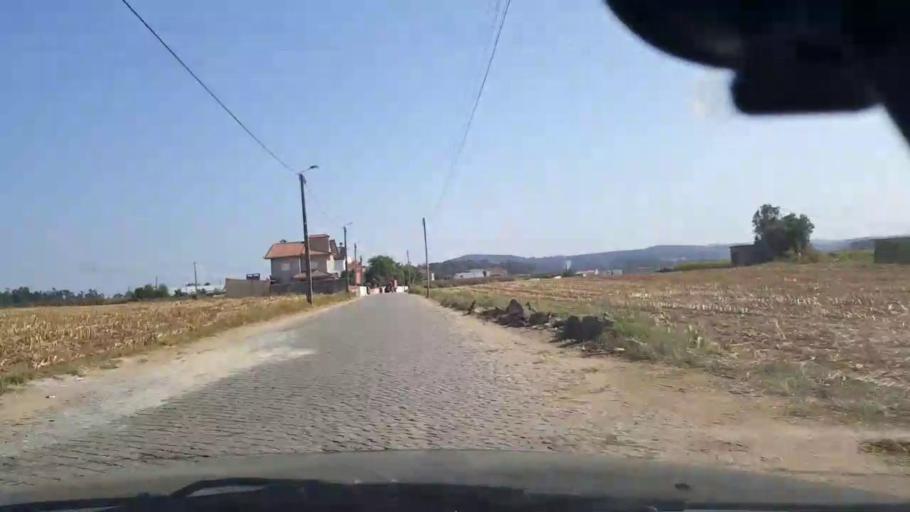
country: PT
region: Porto
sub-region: Povoa de Varzim
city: Pedroso
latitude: 41.4126
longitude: -8.6984
